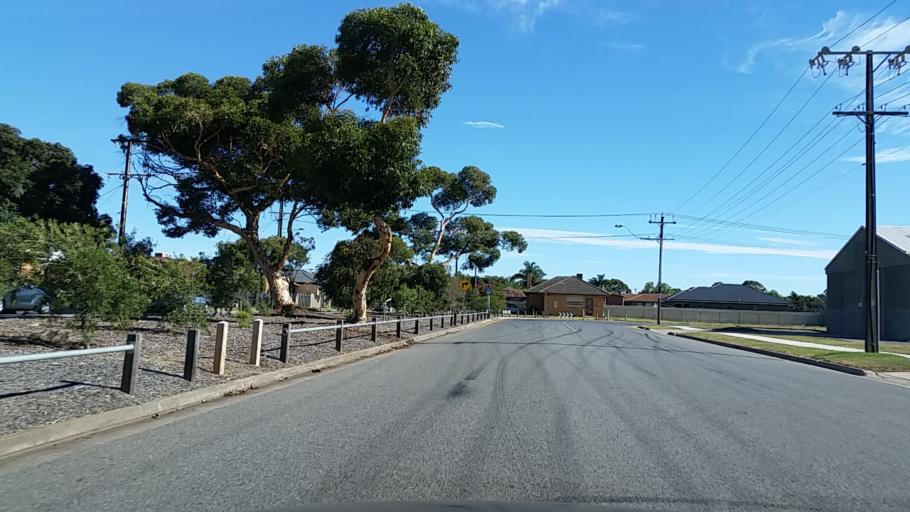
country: AU
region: South Australia
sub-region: Charles Sturt
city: Royal Park
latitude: -34.8676
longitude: 138.5074
